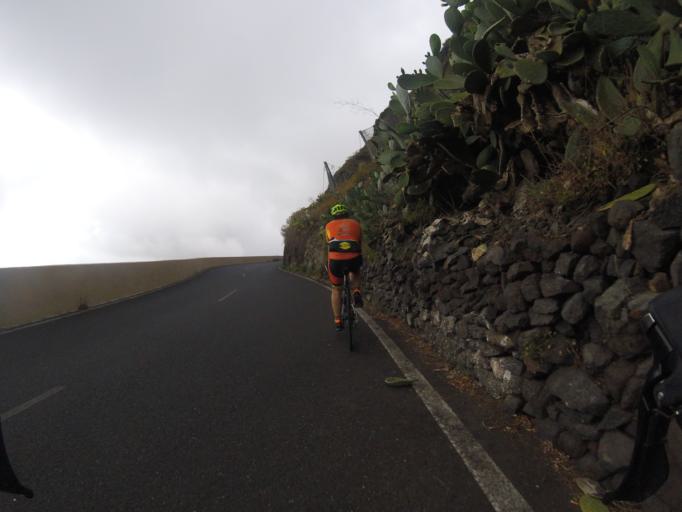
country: ES
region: Canary Islands
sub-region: Provincia de Santa Cruz de Tenerife
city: Guimar
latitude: 28.2953
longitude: -16.4120
